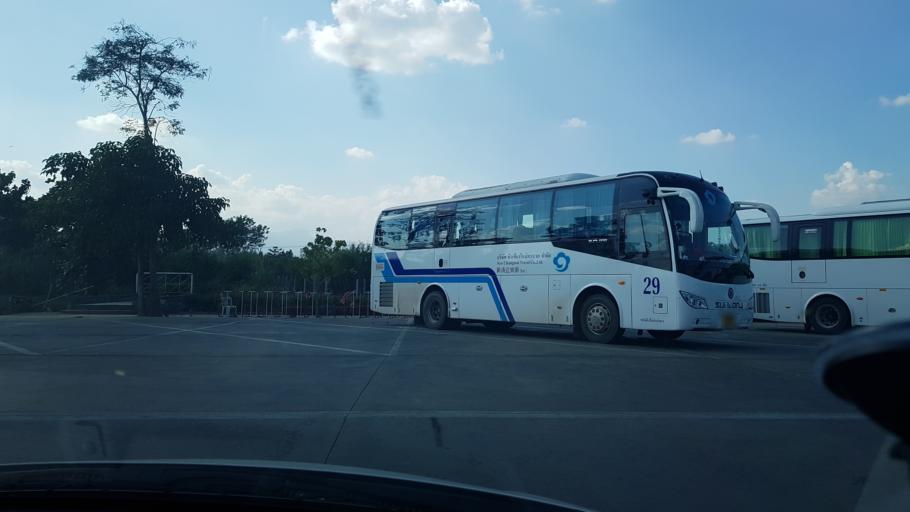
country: TH
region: Chiang Rai
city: Mae Lao
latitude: 19.8233
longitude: 99.7615
